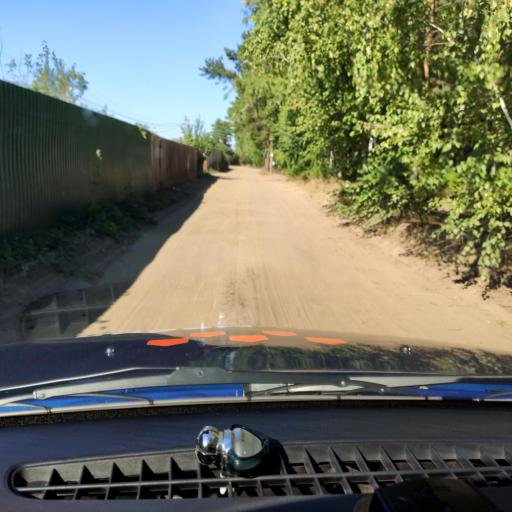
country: RU
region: Voronezj
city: Maslovka
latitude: 51.5459
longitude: 39.1792
